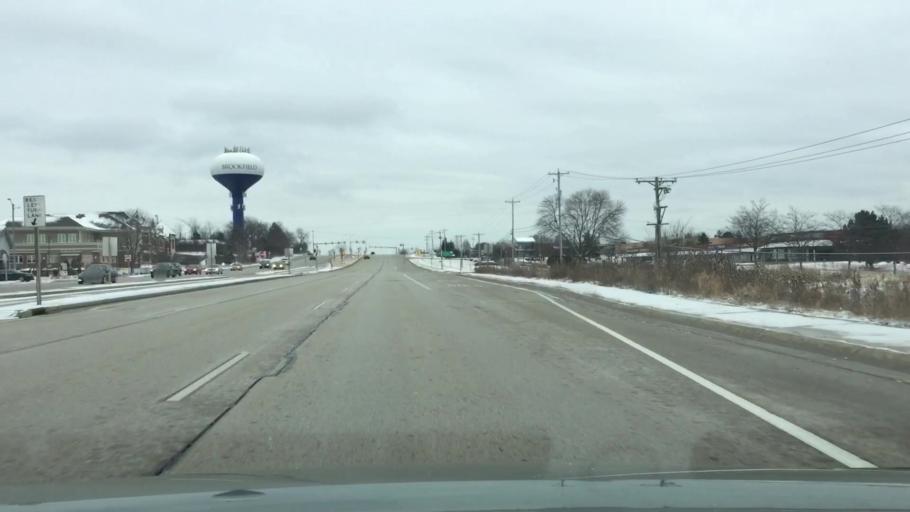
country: US
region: Wisconsin
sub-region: Waukesha County
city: Brookfield
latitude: 43.0902
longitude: -88.1321
